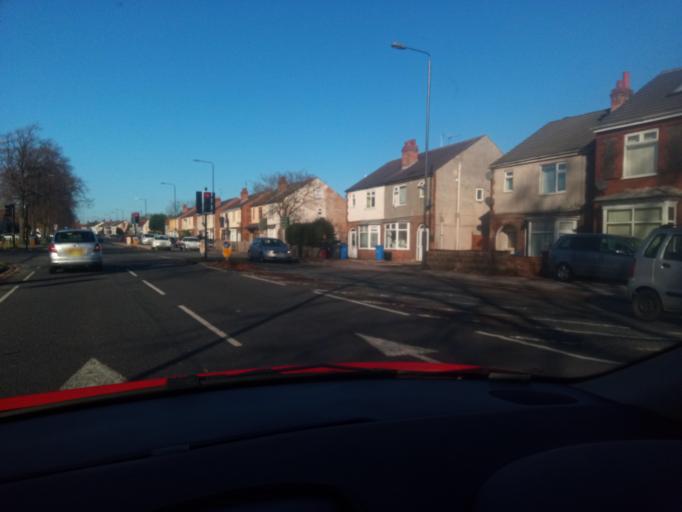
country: GB
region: England
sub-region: Derby
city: Derby
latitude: 52.8927
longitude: -1.4576
